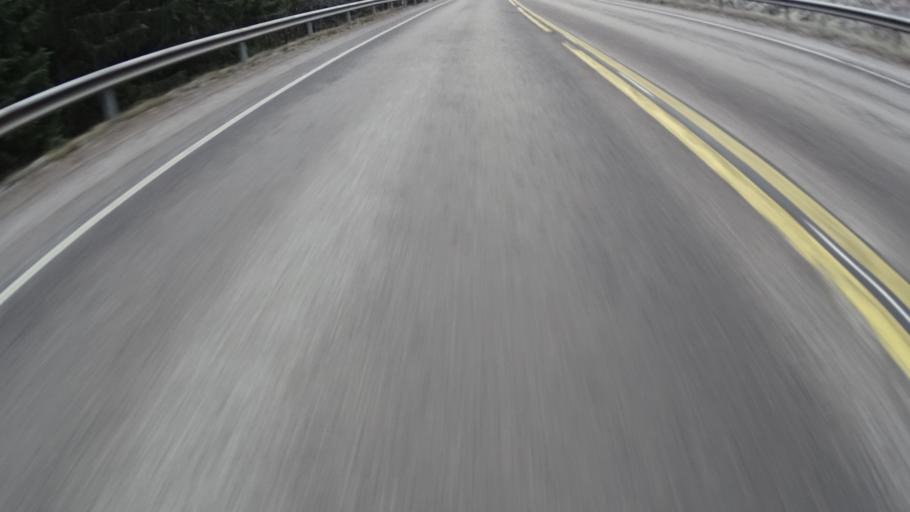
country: FI
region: Uusimaa
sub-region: Helsinki
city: Nurmijaervi
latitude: 60.4153
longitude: 24.7323
